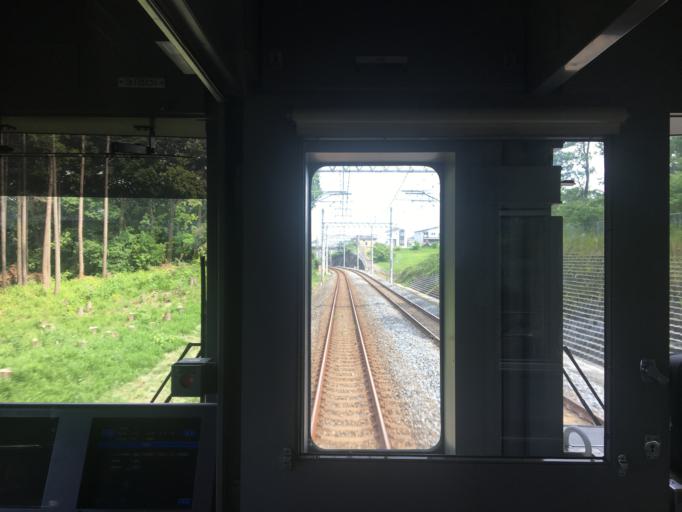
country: JP
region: Saitama
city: Ogawa
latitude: 36.0501
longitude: 139.3164
